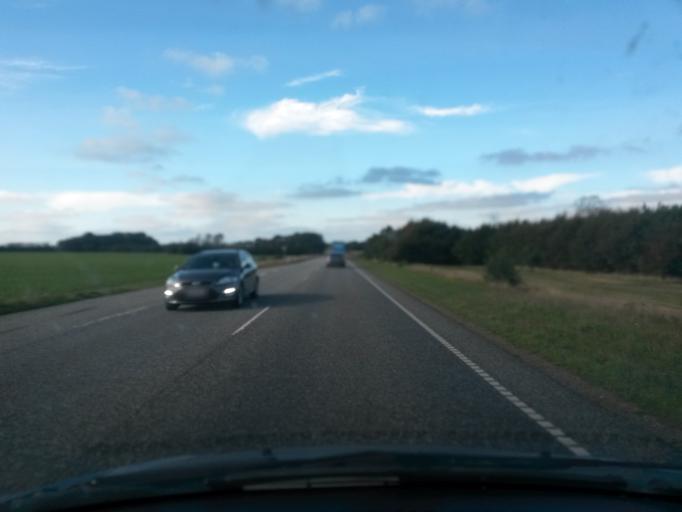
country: DK
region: Central Jutland
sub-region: Holstebro Kommune
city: Holstebro
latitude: 56.3118
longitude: 8.6939
